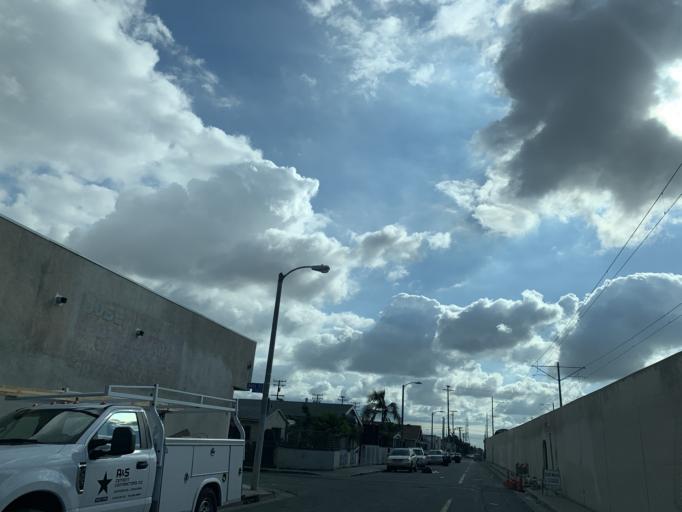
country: US
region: California
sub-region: Los Angeles County
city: Florence-Graham
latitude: 33.9621
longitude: -118.2431
